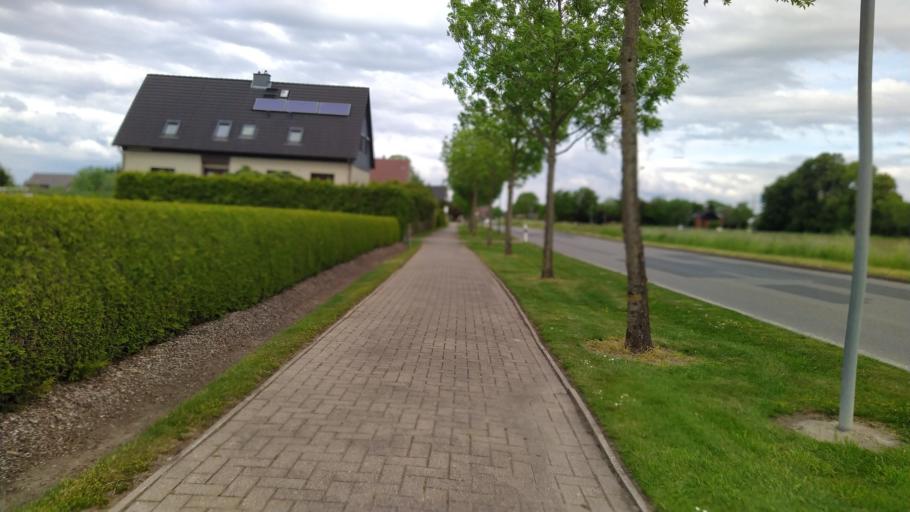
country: DE
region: Lower Saxony
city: Neu Wulmstorf
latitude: 53.4906
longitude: 9.7591
